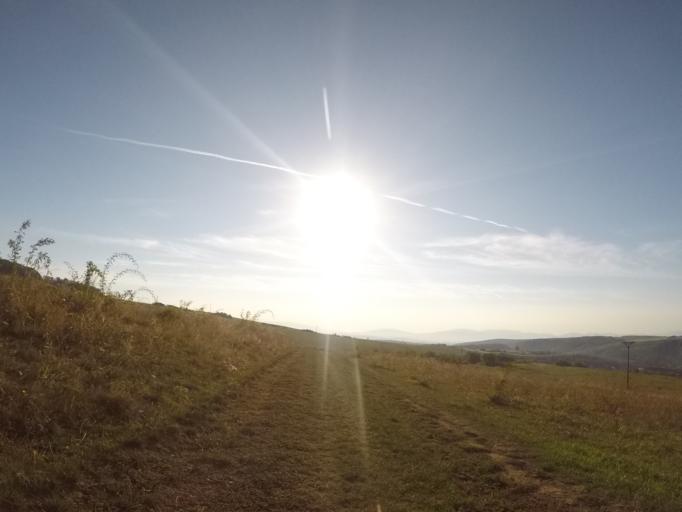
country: SK
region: Kosicky
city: Kosice
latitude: 48.7380
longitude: 21.1339
